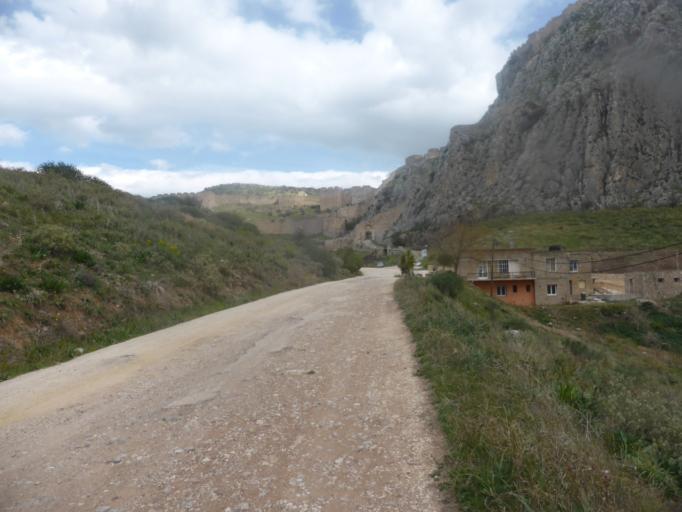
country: GR
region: Peloponnese
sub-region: Nomos Korinthias
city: Arkhaia Korinthos
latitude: 37.8894
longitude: 22.8674
